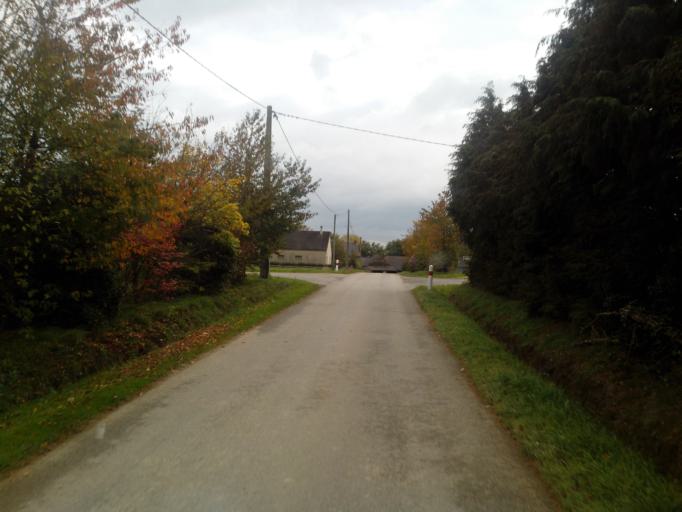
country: FR
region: Brittany
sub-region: Departement du Morbihan
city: Mauron
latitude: 48.0737
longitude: -2.3484
